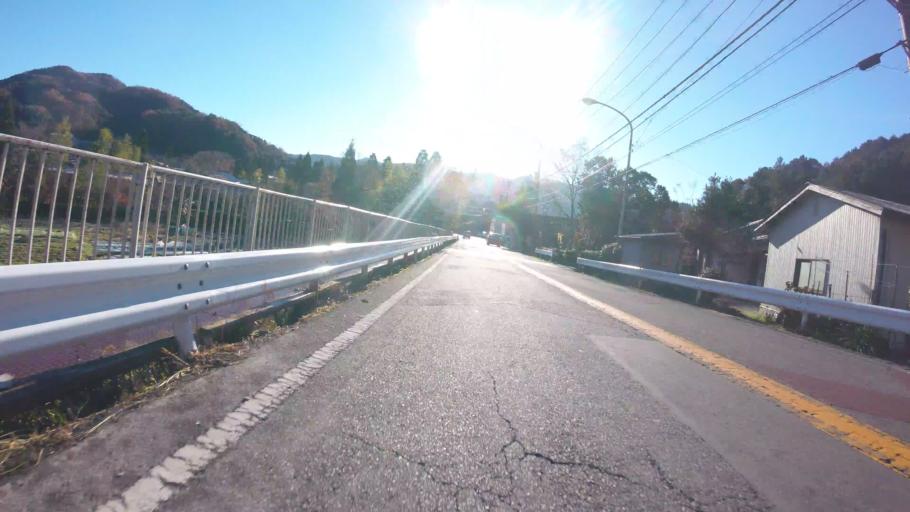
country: JP
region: Shizuoka
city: Heda
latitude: 34.9036
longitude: 138.9235
